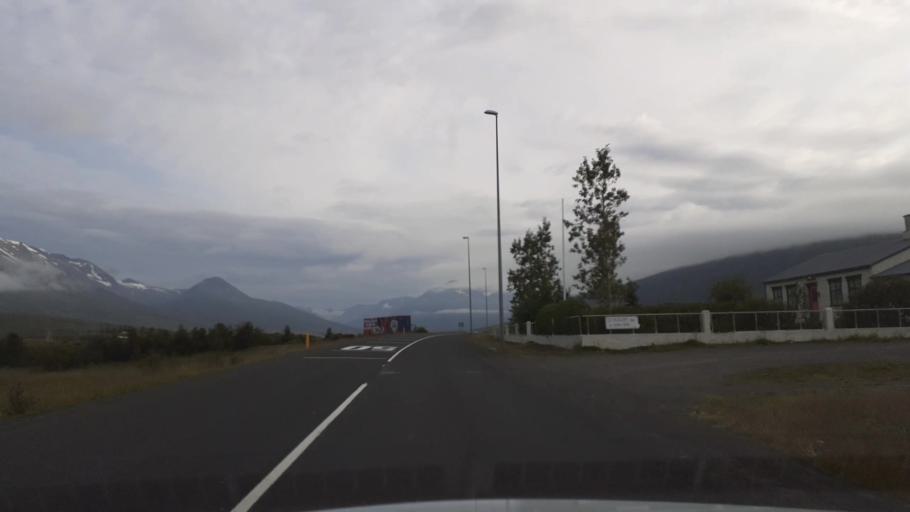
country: IS
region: Northeast
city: Dalvik
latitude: 65.9647
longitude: -18.5334
